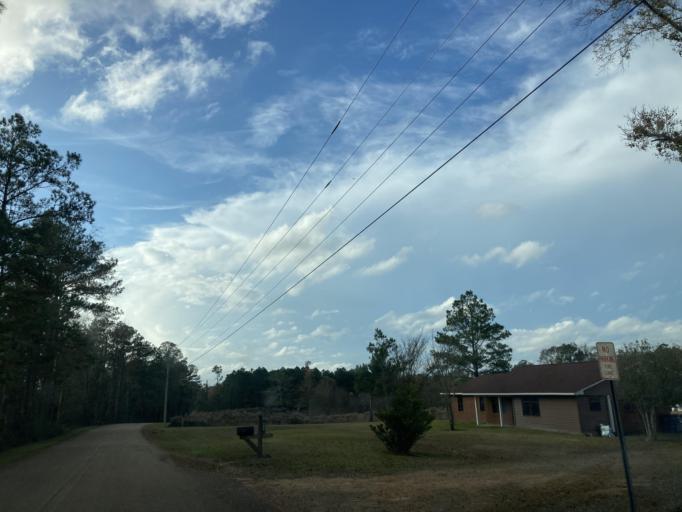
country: US
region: Mississippi
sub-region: Lamar County
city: Purvis
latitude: 31.1416
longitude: -89.6279
